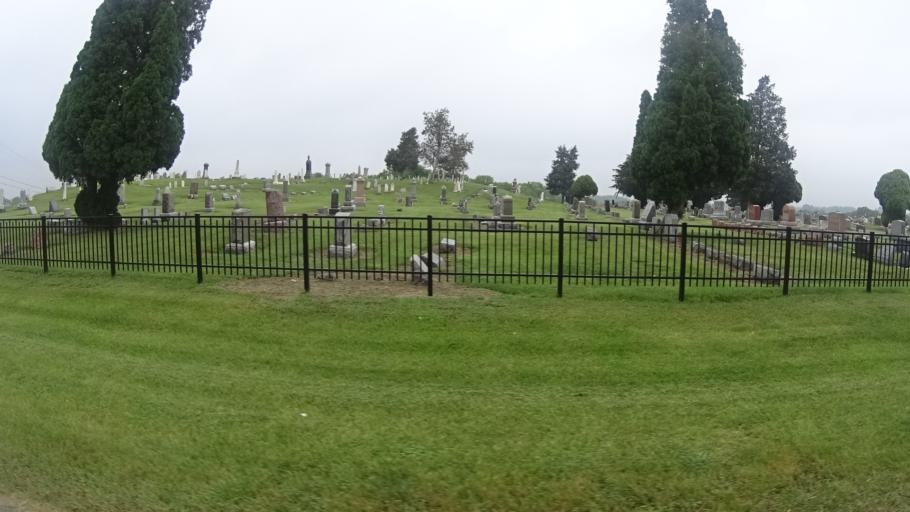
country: US
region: Ohio
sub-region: Erie County
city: Sandusky
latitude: 41.3612
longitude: -82.7588
